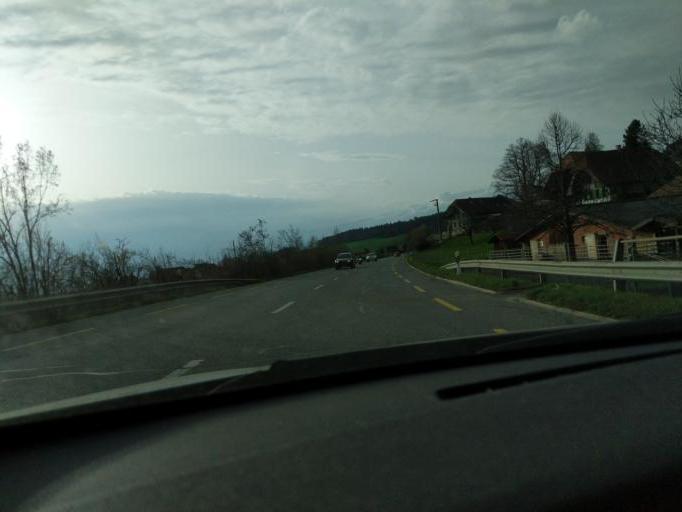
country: CH
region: Bern
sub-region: Bern-Mittelland District
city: Biglen
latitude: 46.9116
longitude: 7.6261
